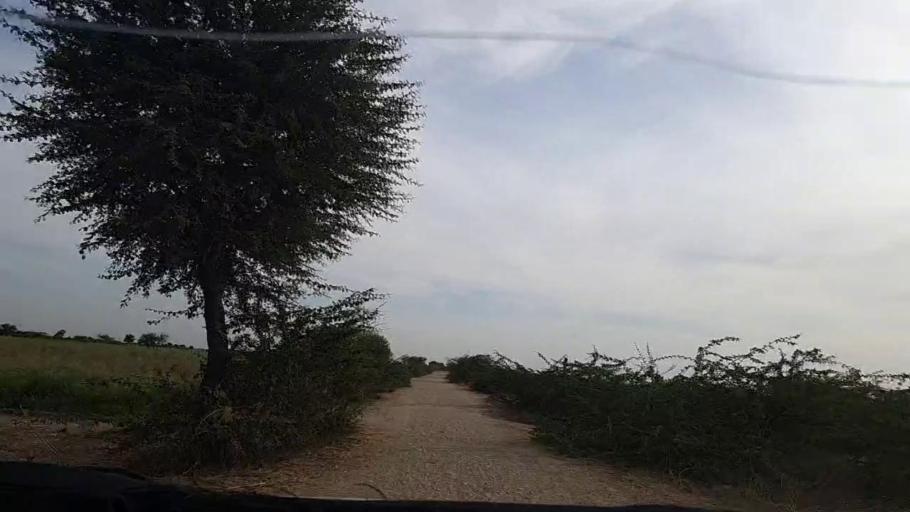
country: PK
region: Sindh
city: Dhoro Naro
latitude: 25.4010
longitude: 69.5176
